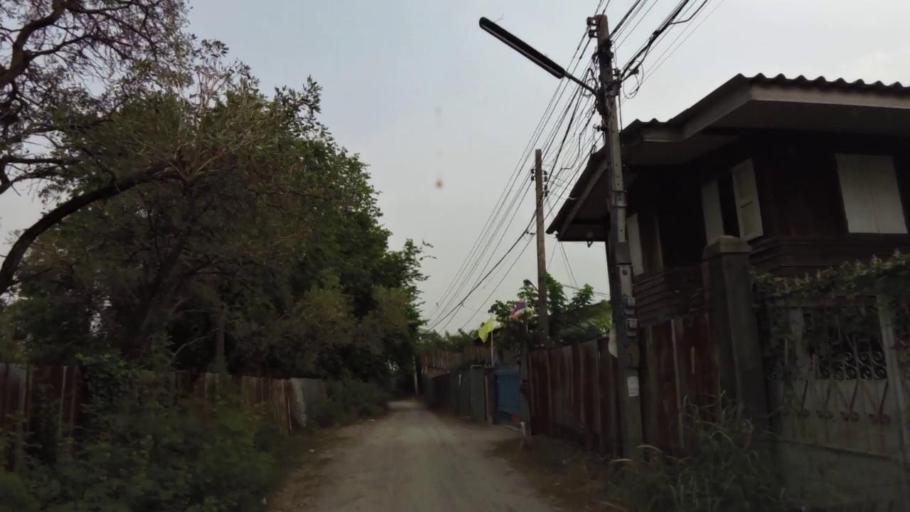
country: TH
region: Phra Nakhon Si Ayutthaya
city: Phra Nakhon Si Ayutthaya
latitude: 14.3495
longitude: 100.5722
